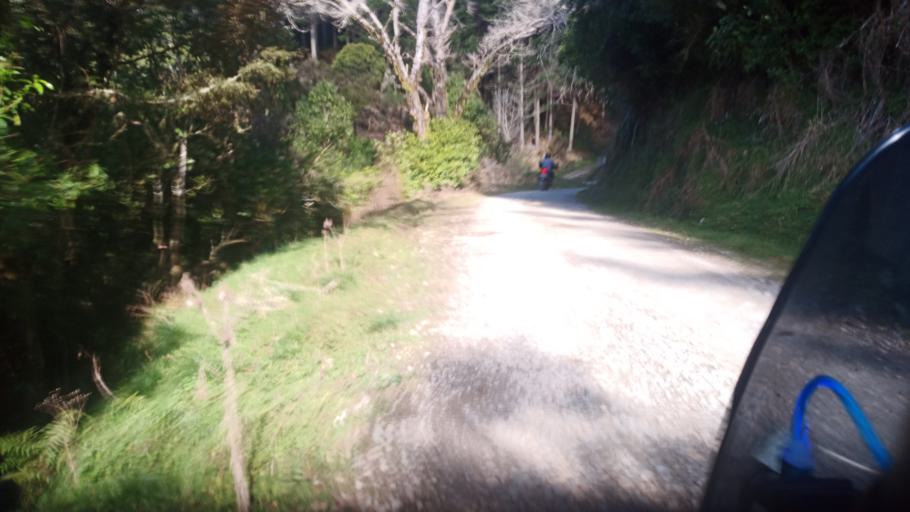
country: NZ
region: Hawke's Bay
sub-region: Wairoa District
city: Wairoa
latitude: -38.6648
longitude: 177.5150
